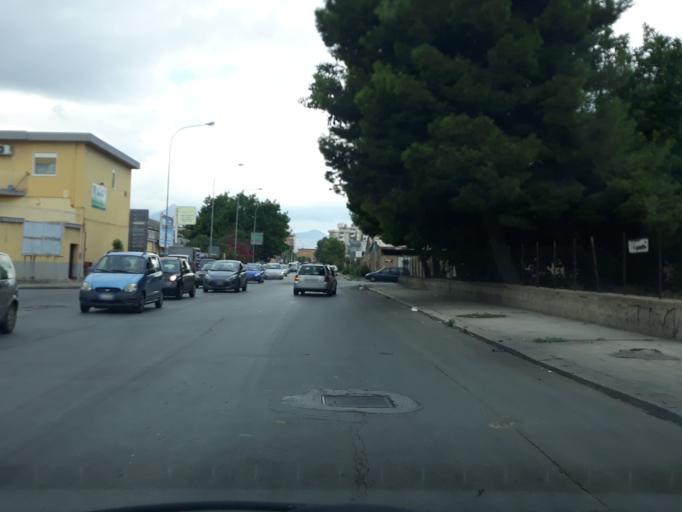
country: IT
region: Sicily
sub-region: Palermo
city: Ciaculli
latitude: 38.0955
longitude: 13.3979
